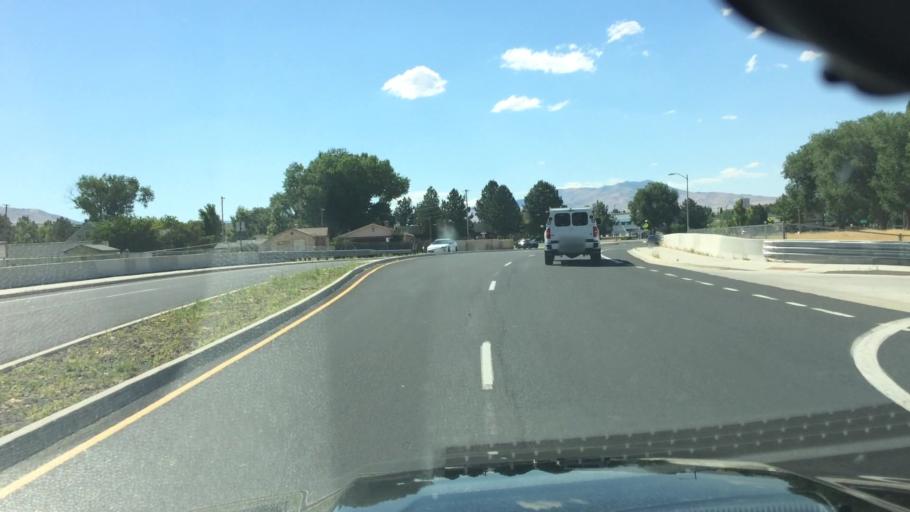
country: US
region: Nevada
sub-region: Washoe County
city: Sparks
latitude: 39.4698
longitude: -119.7725
